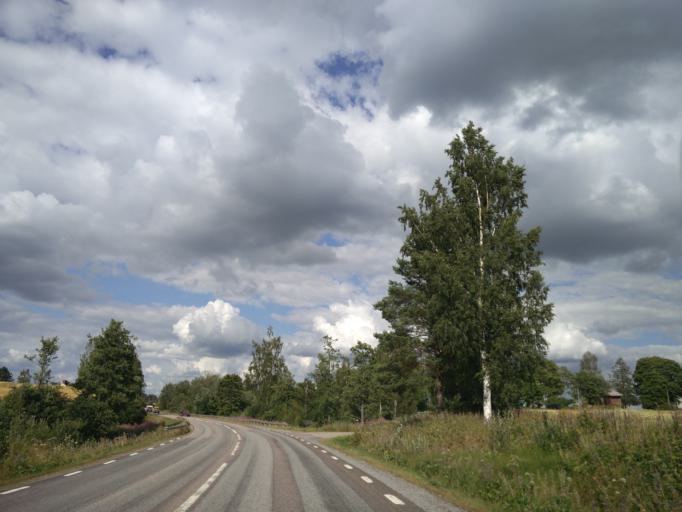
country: SE
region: Vaermland
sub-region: Sunne Kommun
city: Sunne
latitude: 59.7226
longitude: 13.1173
